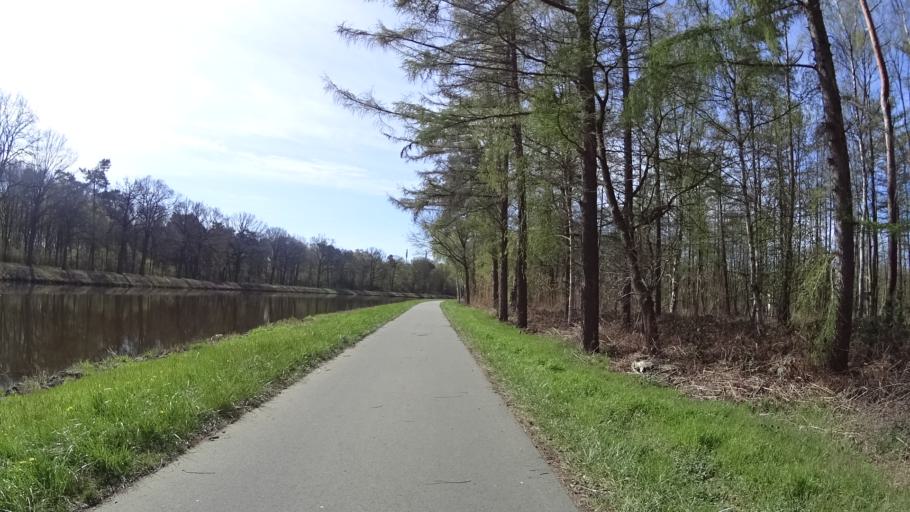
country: DE
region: Lower Saxony
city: Lingen
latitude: 52.5710
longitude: 7.3096
